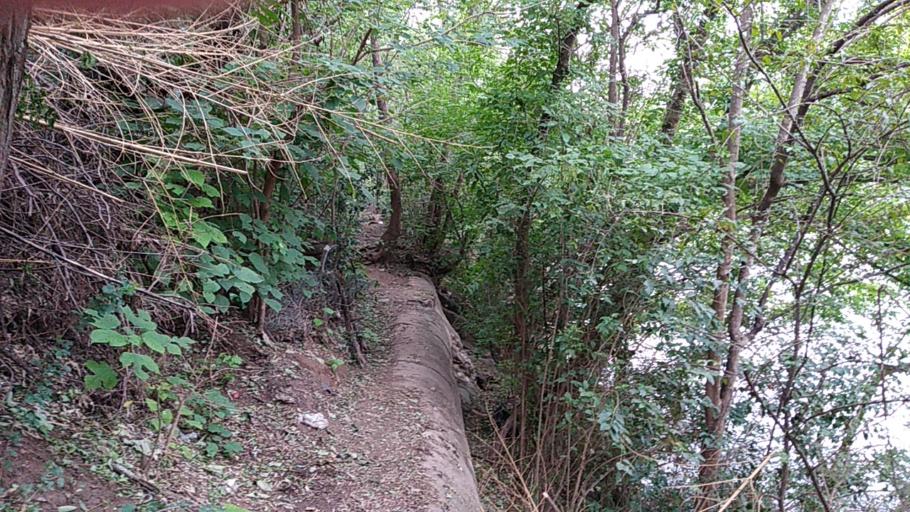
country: AR
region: Cordoba
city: Alta Gracia
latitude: -31.7246
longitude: -64.4341
